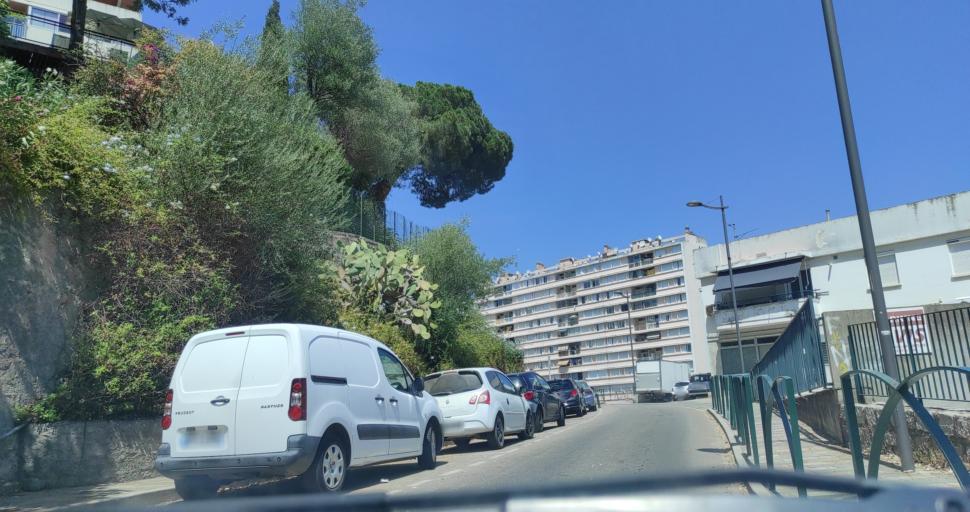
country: FR
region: Corsica
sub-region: Departement de la Corse-du-Sud
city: Ajaccio
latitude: 41.9335
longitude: 8.7406
